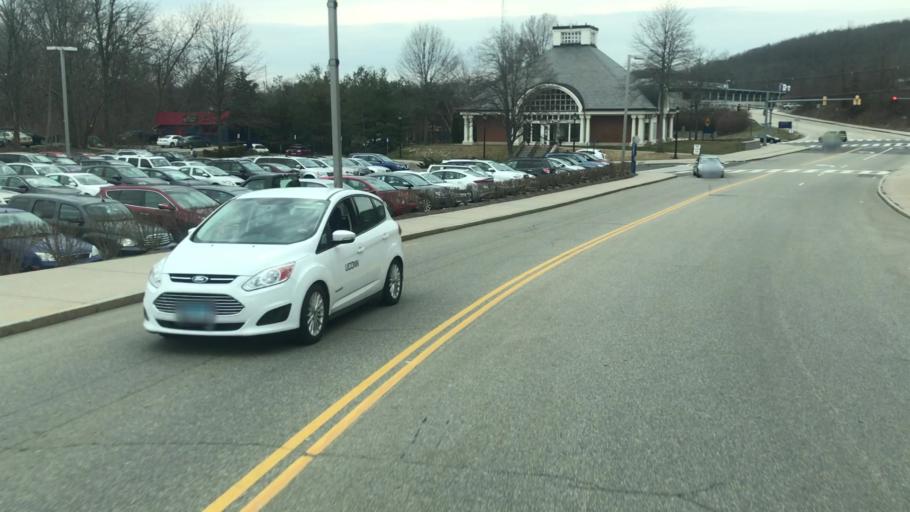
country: US
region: Connecticut
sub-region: Tolland County
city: Storrs
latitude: 41.8085
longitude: -72.2587
